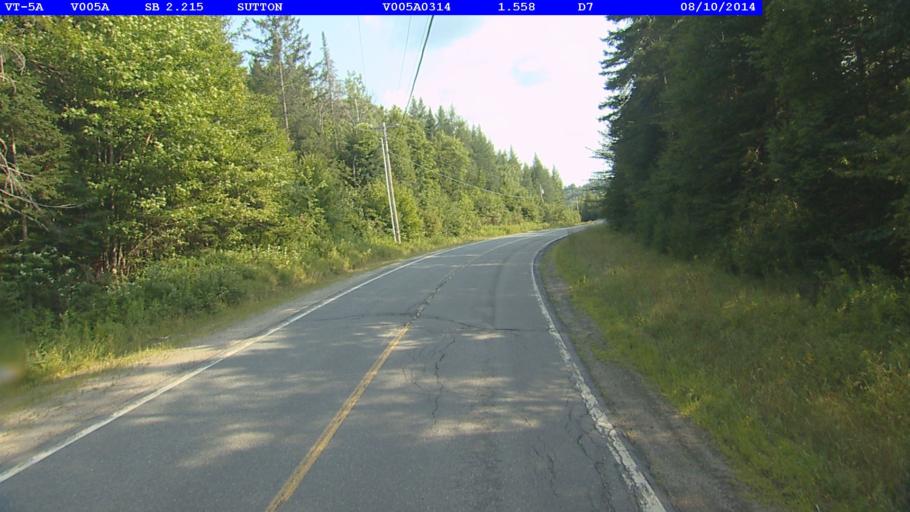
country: US
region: Vermont
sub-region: Caledonia County
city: Lyndonville
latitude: 44.6696
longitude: -71.9938
